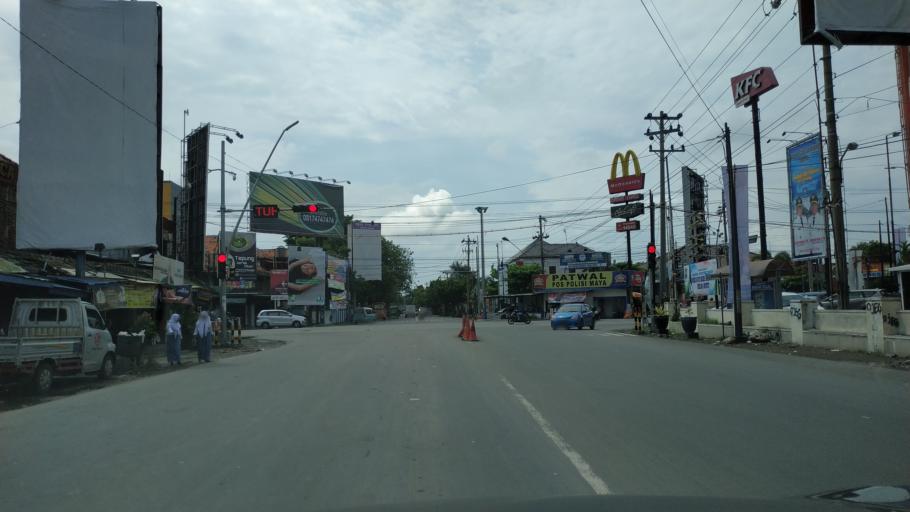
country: ID
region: Central Java
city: Tegal
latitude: -6.8698
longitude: 109.1283
